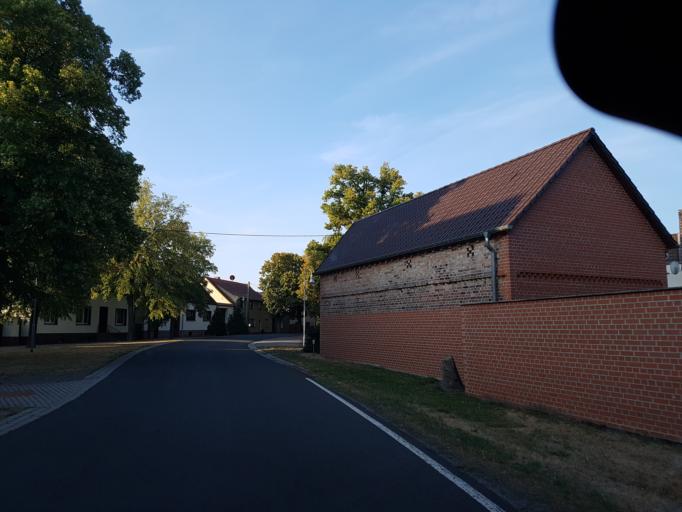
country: DE
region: Saxony-Anhalt
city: Holzdorf
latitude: 51.8325
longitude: 13.1255
